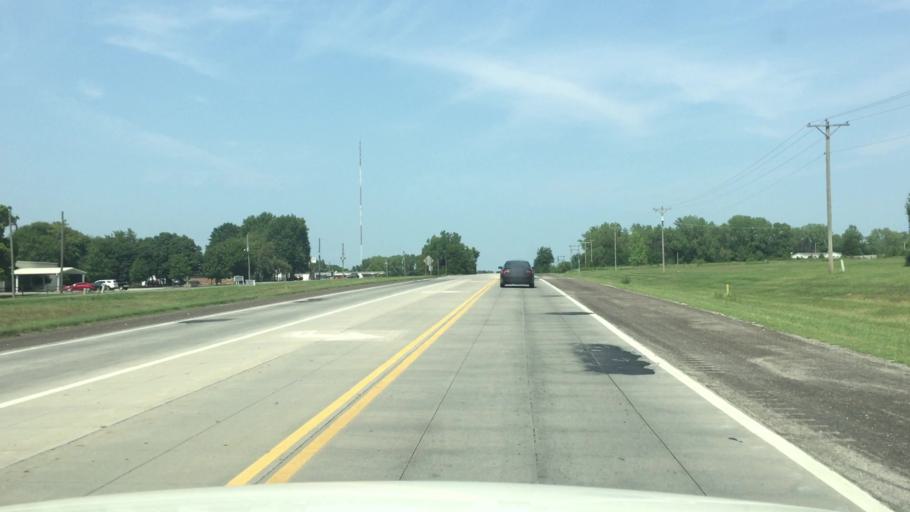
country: US
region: Kansas
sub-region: Crawford County
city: Pittsburg
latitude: 37.4266
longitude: -94.7156
